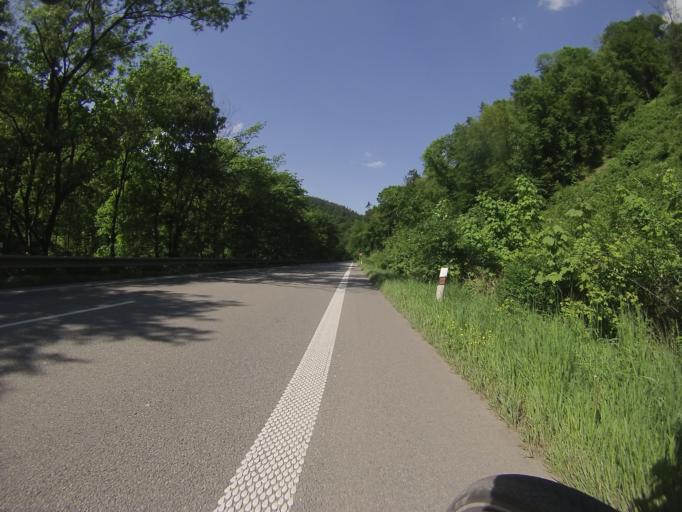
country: CZ
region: South Moravian
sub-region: Okres Blansko
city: Adamov
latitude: 49.3310
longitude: 16.6442
